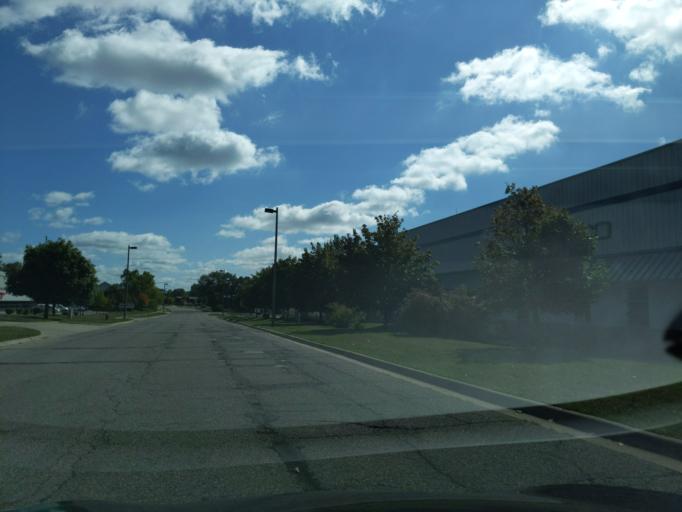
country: US
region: Michigan
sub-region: Ingham County
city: Holt
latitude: 42.6807
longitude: -84.5131
